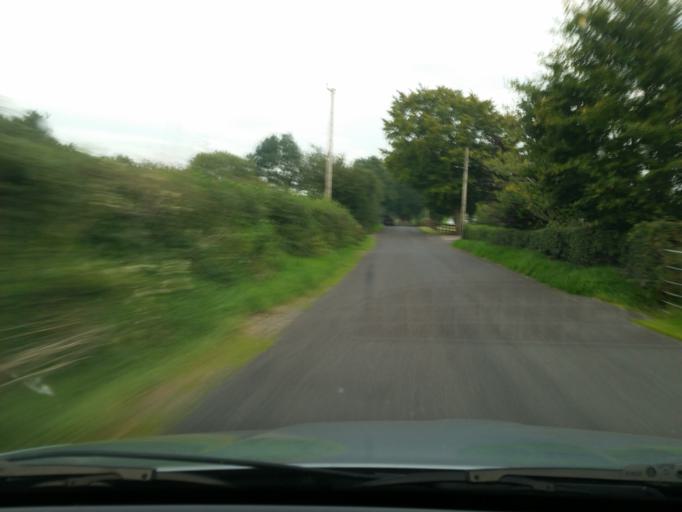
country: GB
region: Northern Ireland
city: Fivemiletown
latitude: 54.3742
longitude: -7.3055
